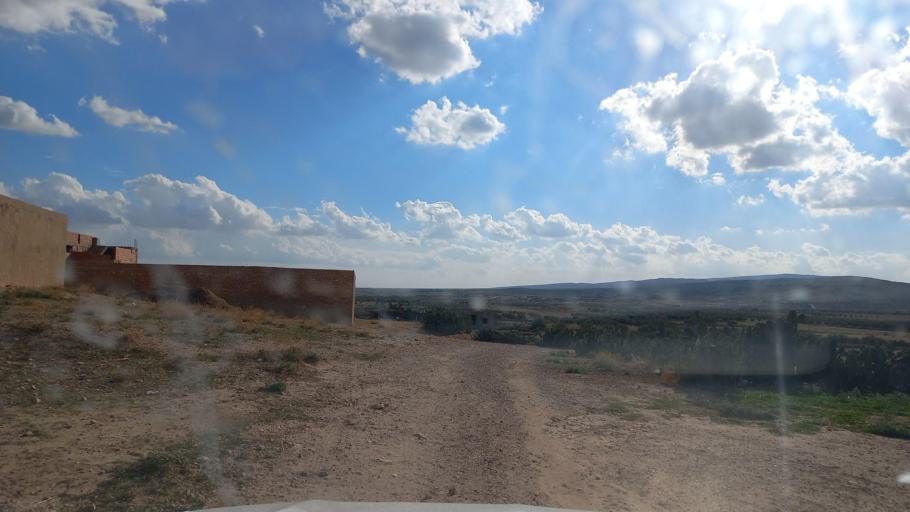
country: TN
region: Al Qasrayn
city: Sbiba
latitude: 35.3915
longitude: 9.0421
